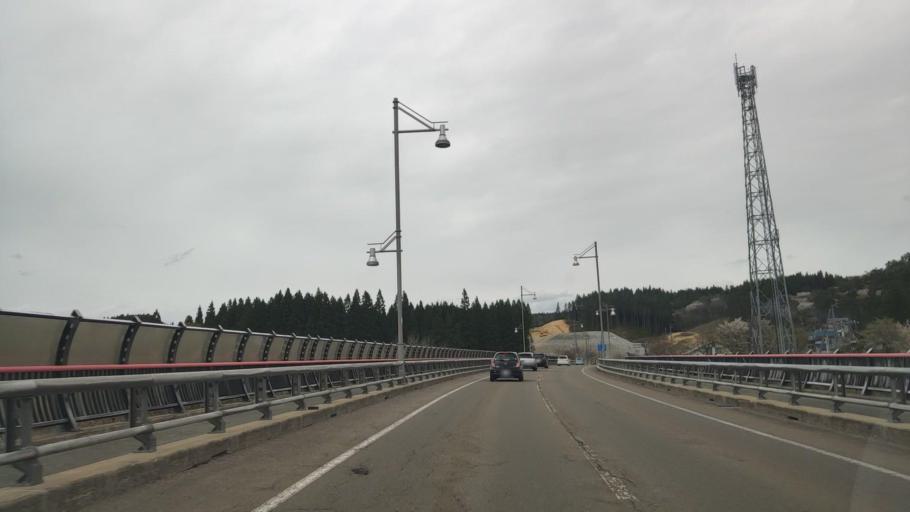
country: JP
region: Akita
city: Takanosu
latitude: 40.2104
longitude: 140.3019
